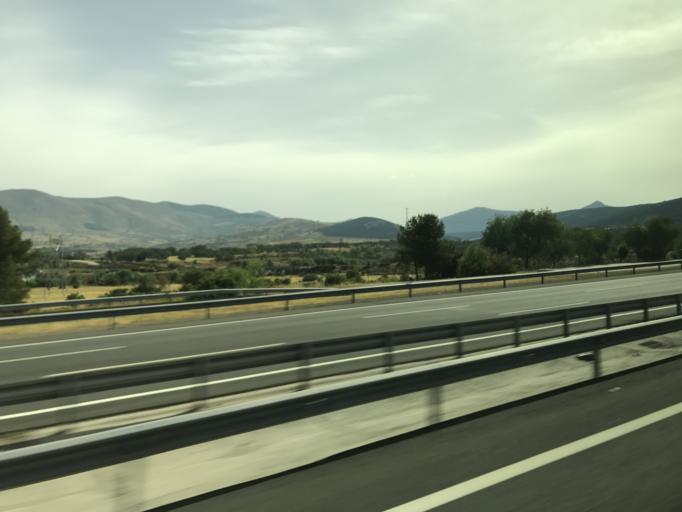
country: ES
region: Castille and Leon
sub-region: Provincia de Segovia
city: Otero de Herreros
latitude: 40.7360
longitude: -4.2079
